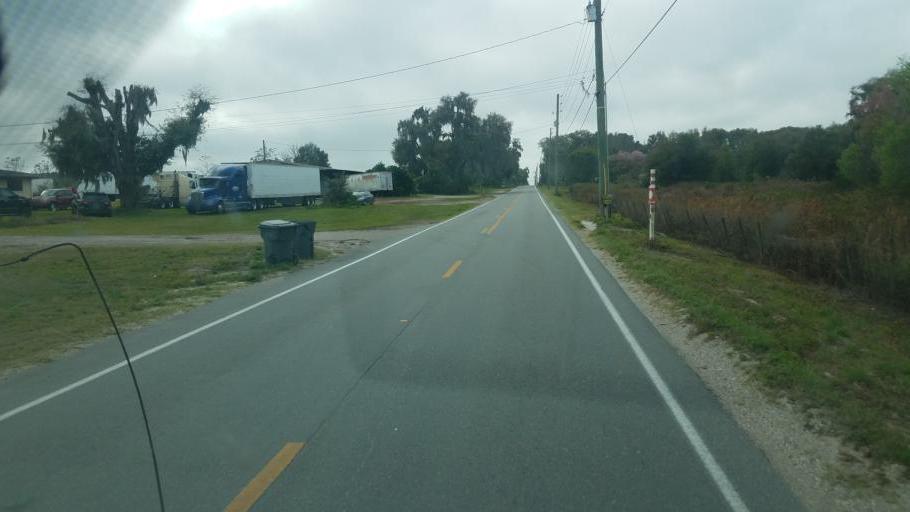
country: US
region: Florida
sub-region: Polk County
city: Kathleen
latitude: 28.1474
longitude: -82.0233
